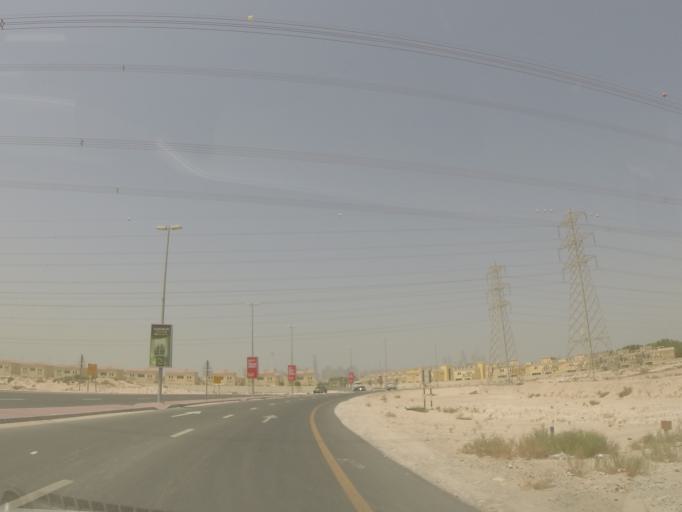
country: AE
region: Dubai
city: Dubai
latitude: 25.0398
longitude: 55.1720
